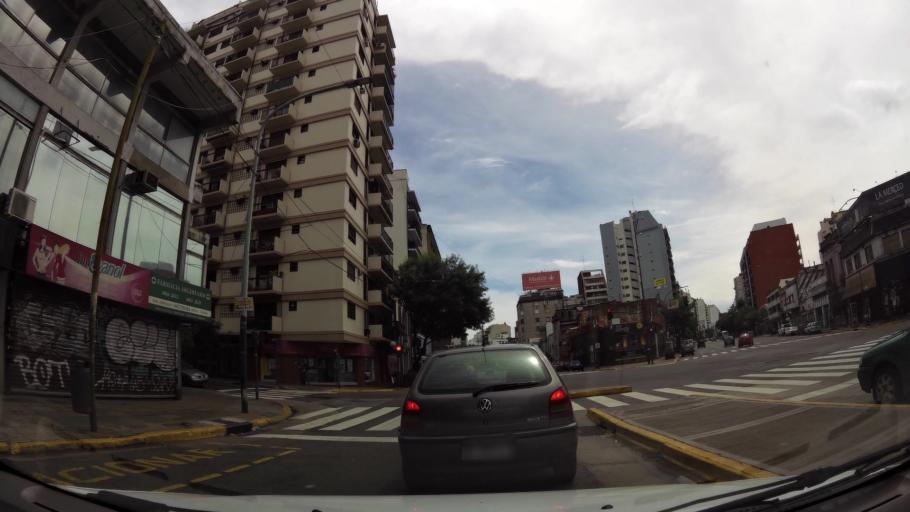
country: AR
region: Buenos Aires F.D.
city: Colegiales
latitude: -34.5979
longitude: -58.4232
